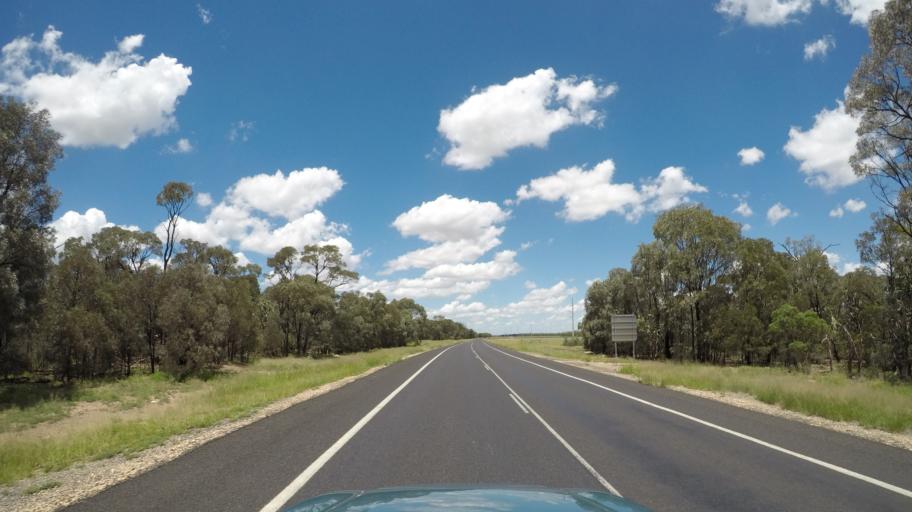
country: AU
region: Queensland
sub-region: Goondiwindi
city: Goondiwindi
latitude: -28.1081
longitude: 150.7203
